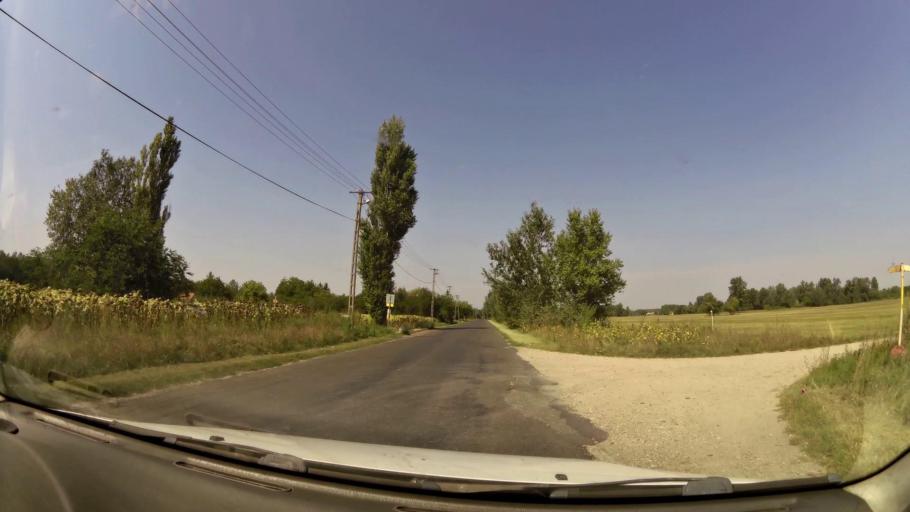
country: HU
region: Pest
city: Tapioszentmarton
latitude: 47.3385
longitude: 19.7926
